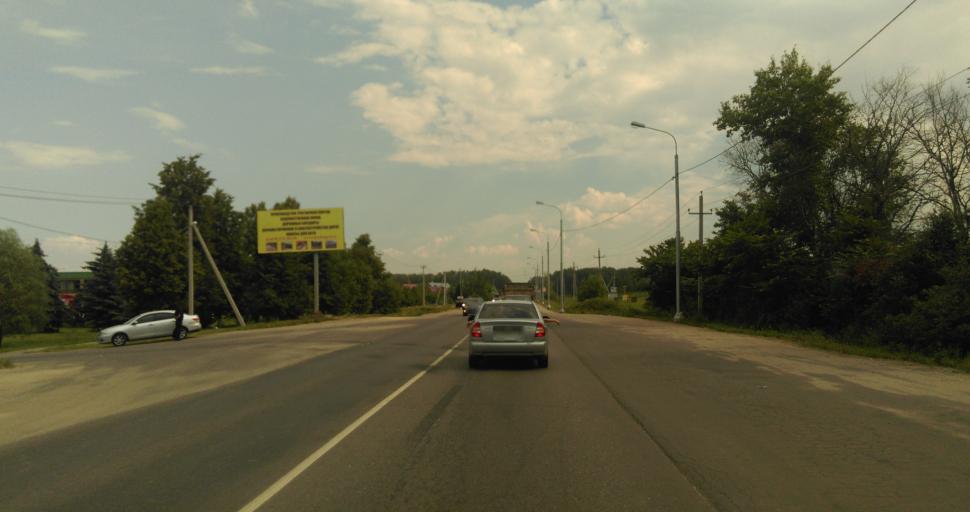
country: RU
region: Moskovskaya
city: Zhitnevo
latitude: 55.3415
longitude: 37.9061
